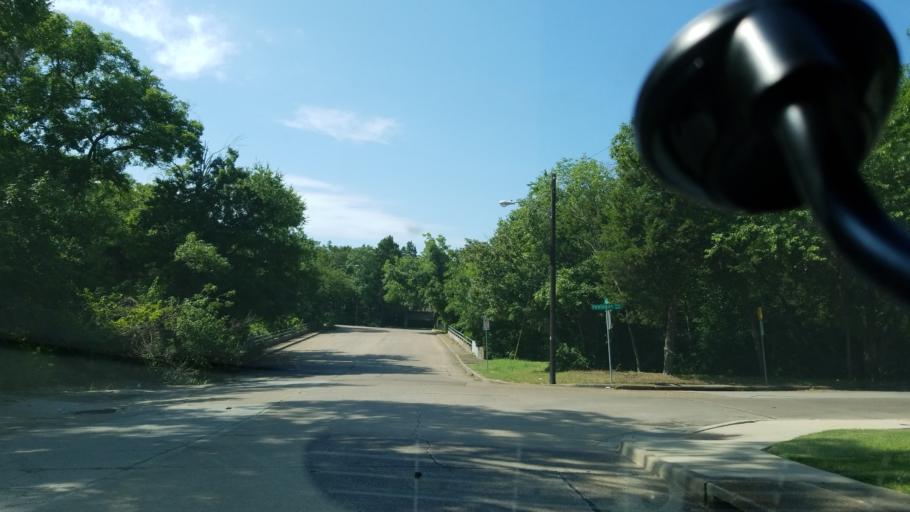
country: US
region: Texas
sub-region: Dallas County
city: Cockrell Hill
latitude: 32.7060
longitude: -96.8659
